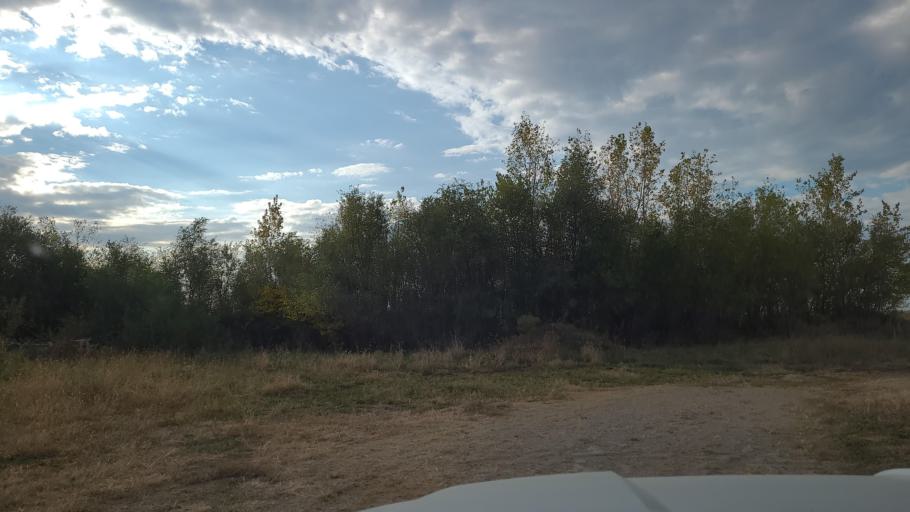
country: US
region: Kansas
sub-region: Douglas County
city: Lawrence
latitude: 39.0136
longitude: -95.2100
